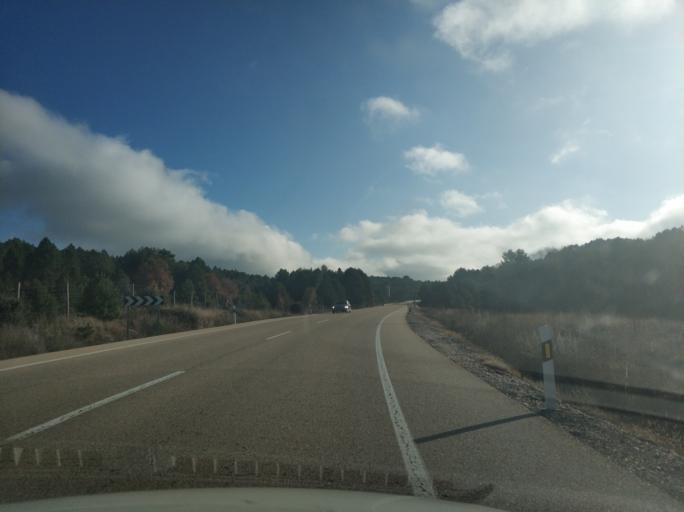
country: ES
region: Castille and Leon
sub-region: Provincia de Soria
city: Navaleno
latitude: 41.8401
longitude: -3.0244
